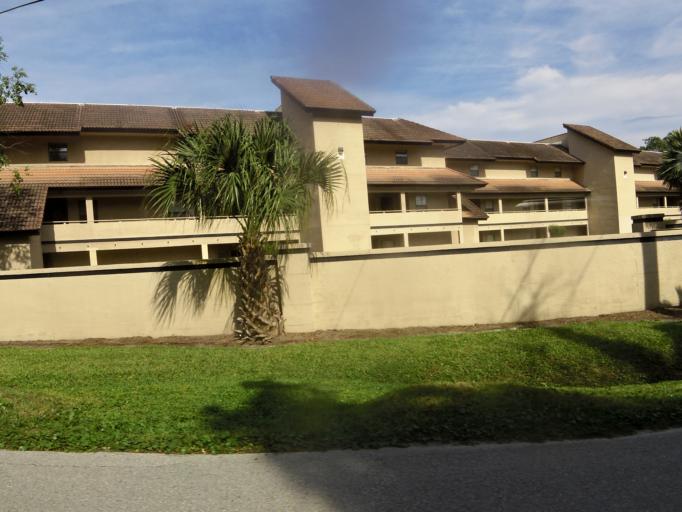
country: US
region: Florida
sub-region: Duval County
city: Jacksonville
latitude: 30.3140
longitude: -81.5966
